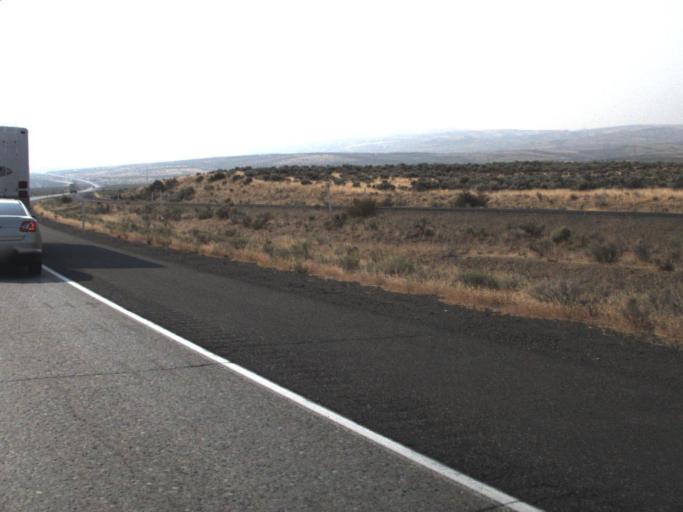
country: US
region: Washington
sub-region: Kittitas County
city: Kittitas
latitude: 46.8419
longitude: -120.3753
